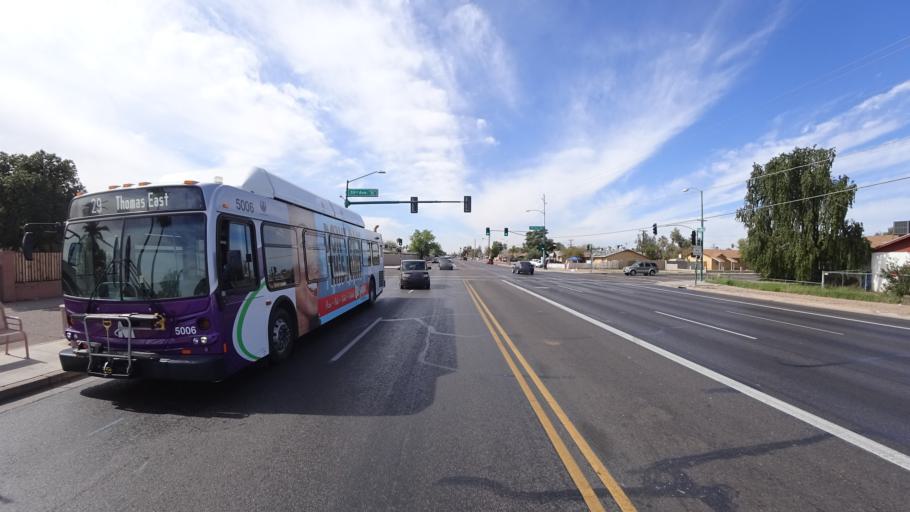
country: US
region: Arizona
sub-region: Maricopa County
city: Glendale
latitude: 33.4805
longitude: -112.1776
